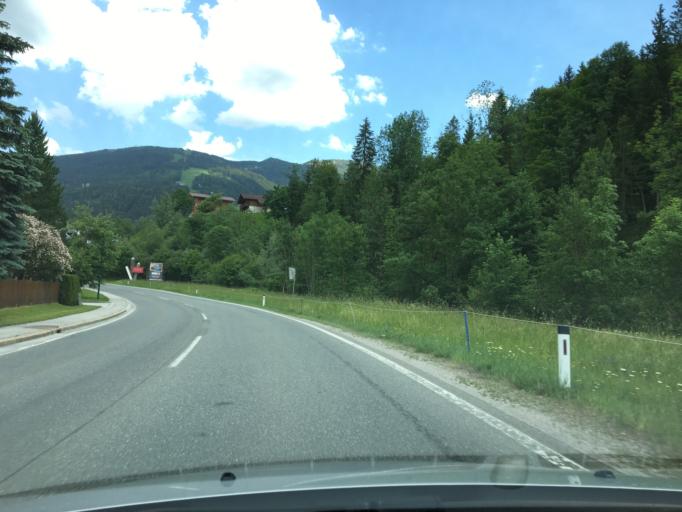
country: AT
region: Salzburg
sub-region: Politischer Bezirk Sankt Johann im Pongau
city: Wagrain
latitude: 47.3348
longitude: 13.2879
